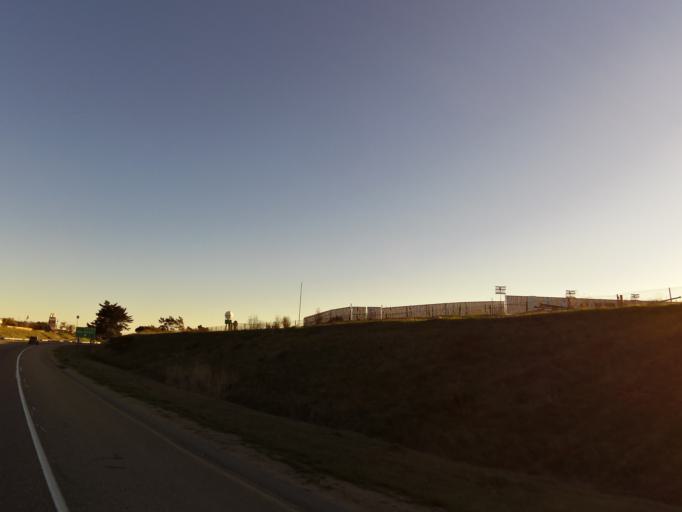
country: US
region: California
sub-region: Monterey County
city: Gonzales
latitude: 36.5176
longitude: -121.4408
